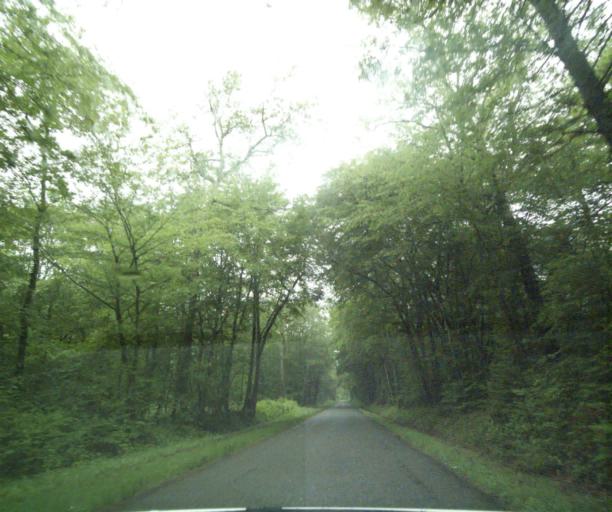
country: FR
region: Bourgogne
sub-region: Departement de Saone-et-Loire
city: Paray-le-Monial
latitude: 46.4248
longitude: 4.1871
